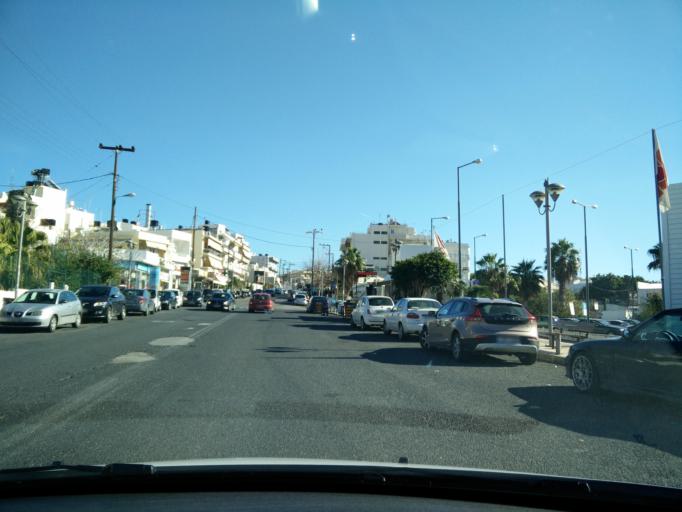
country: GR
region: Crete
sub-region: Nomos Irakleiou
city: Nea Alikarnassos
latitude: 35.3393
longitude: 25.1547
